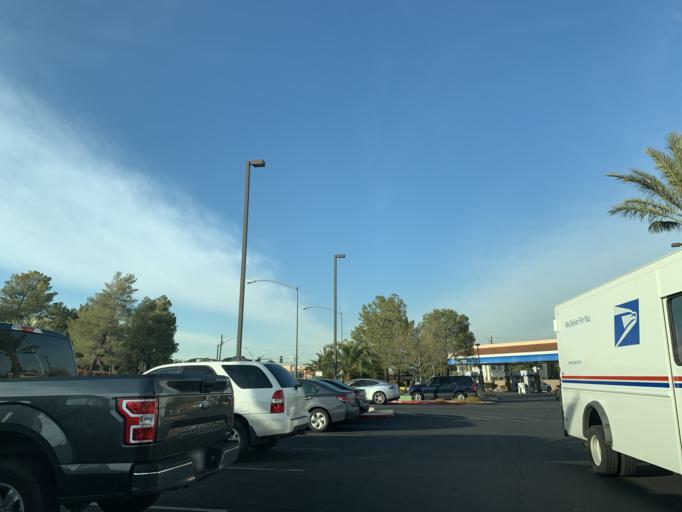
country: US
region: Nevada
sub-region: Clark County
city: Spring Valley
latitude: 36.0987
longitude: -115.2427
